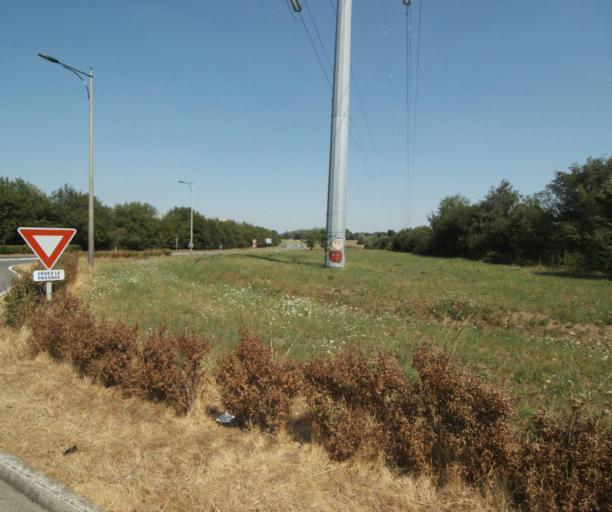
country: FR
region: Nord-Pas-de-Calais
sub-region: Departement du Nord
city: Bousbecque
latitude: 50.7664
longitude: 3.0871
